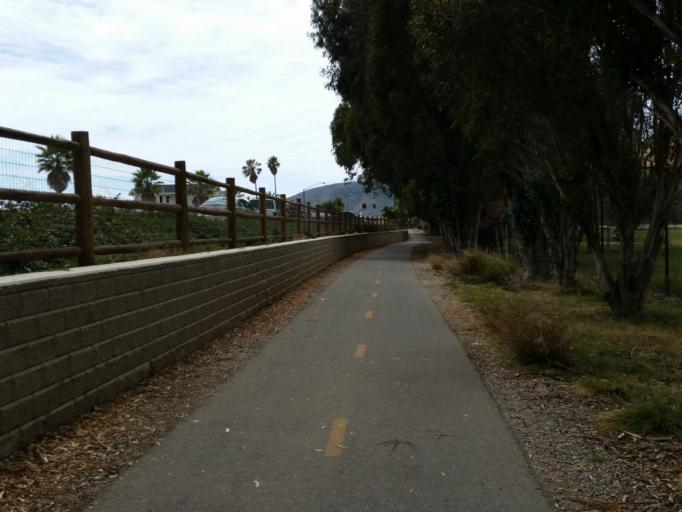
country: US
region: California
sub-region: San Luis Obispo County
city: Avila Beach
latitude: 35.1816
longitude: -120.7341
